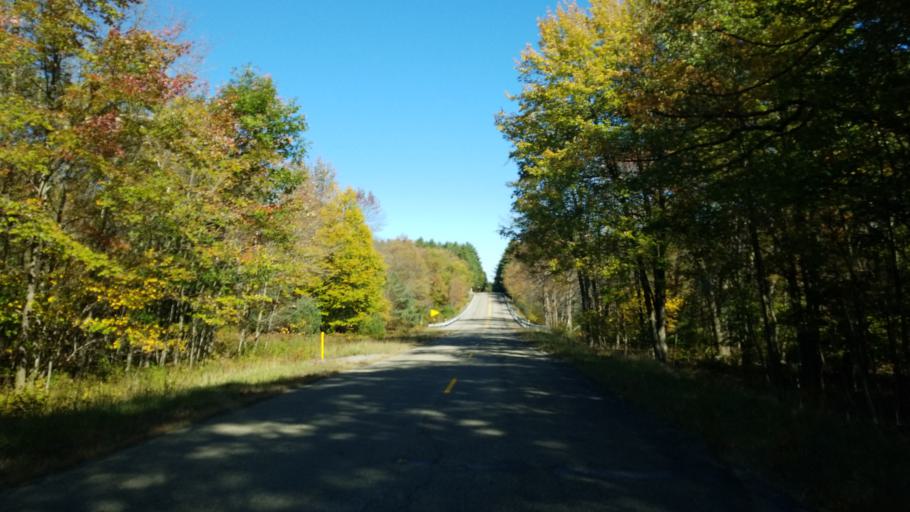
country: US
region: Pennsylvania
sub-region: Clearfield County
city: Shiloh
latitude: 41.2596
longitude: -78.3078
